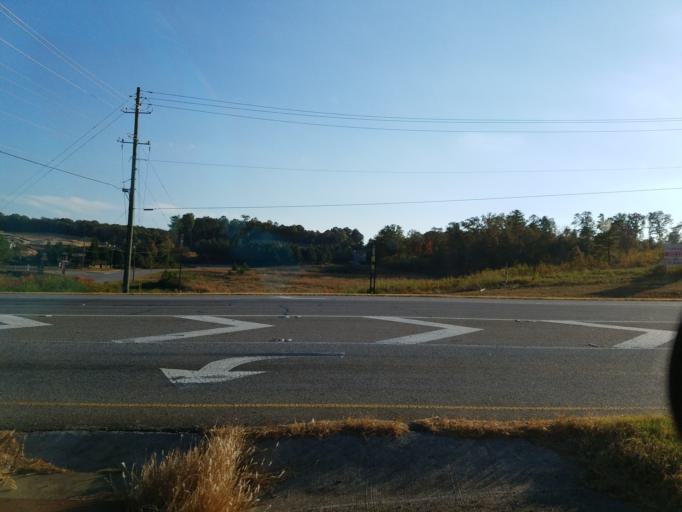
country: US
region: Georgia
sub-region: Bartow County
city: Cartersville
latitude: 34.2186
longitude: -84.8717
